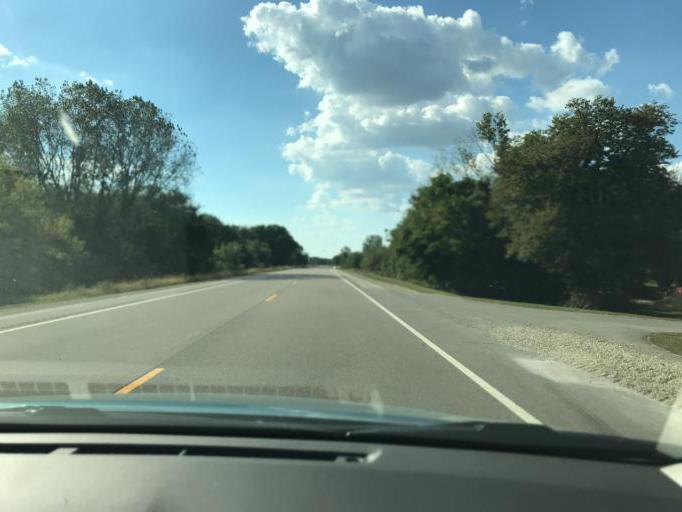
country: US
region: Wisconsin
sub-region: Green County
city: Brodhead
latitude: 42.5731
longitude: -89.3581
